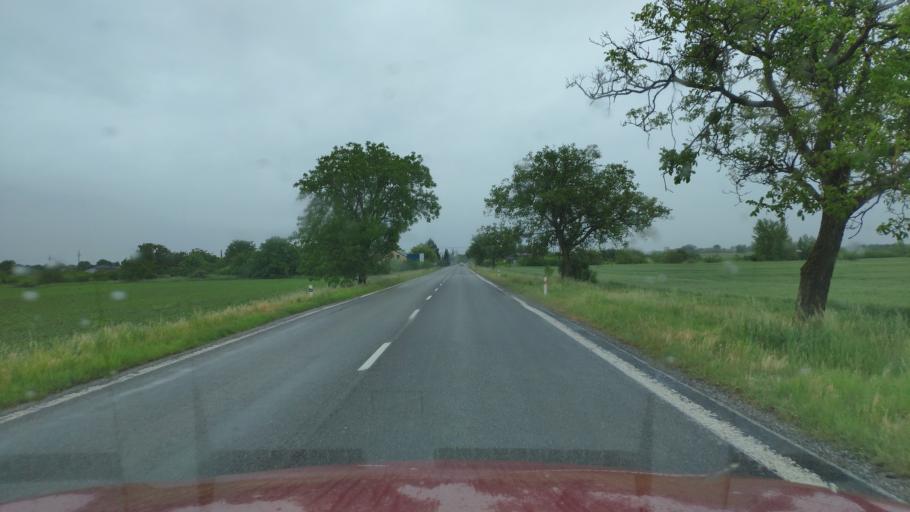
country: HU
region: Borsod-Abauj-Zemplen
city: Karcsa
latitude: 48.4251
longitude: 21.8420
